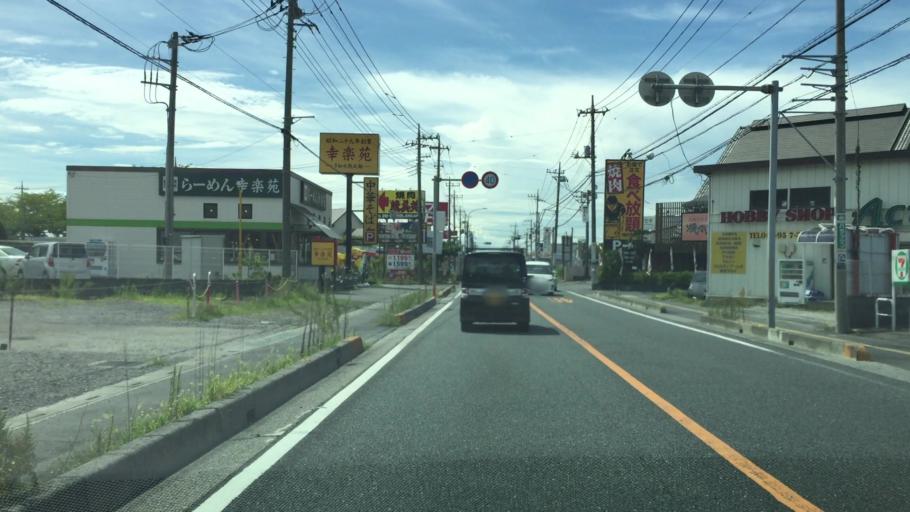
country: JP
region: Chiba
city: Nagareyama
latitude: 35.8482
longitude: 139.8679
